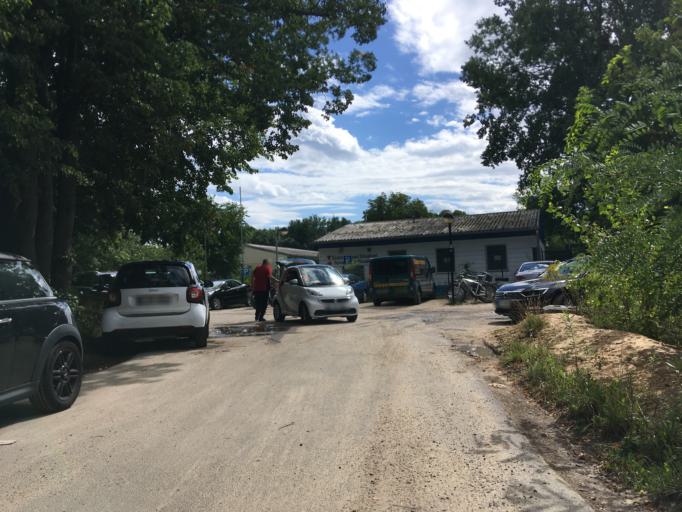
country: DE
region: Berlin
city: Staaken
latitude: 52.5342
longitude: 13.1310
